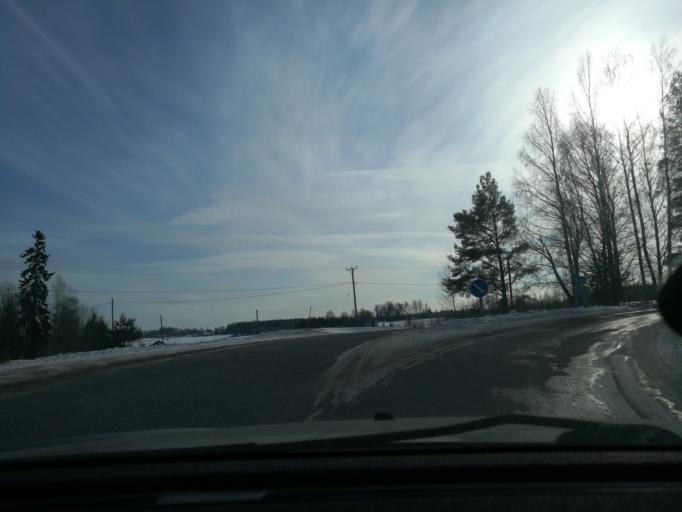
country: FI
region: Uusimaa
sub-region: Helsinki
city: Saukkola
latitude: 60.4349
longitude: 24.0176
